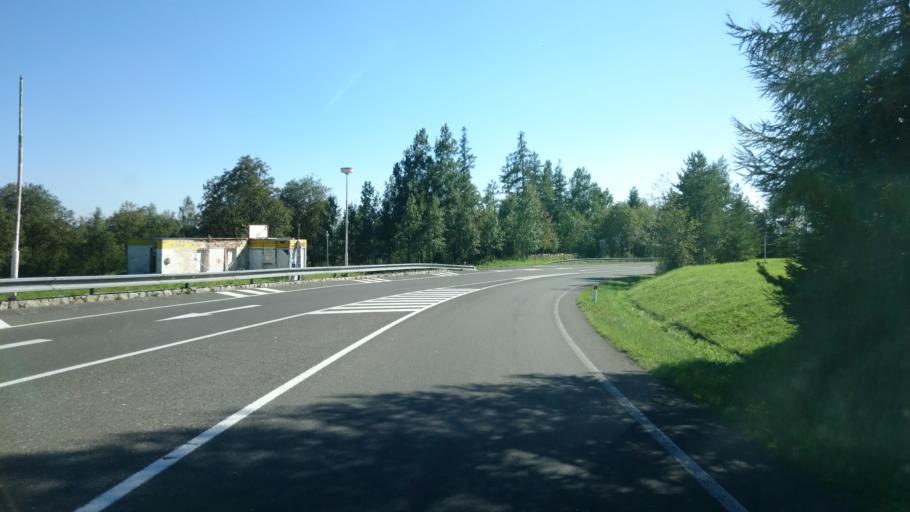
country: SK
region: Presovsky
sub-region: Okres Poprad
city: Nova Lesna
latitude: 49.1727
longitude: 20.2941
